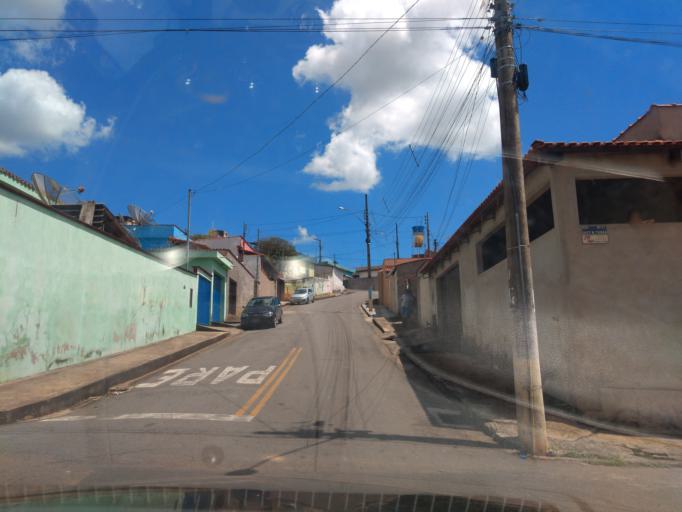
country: BR
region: Minas Gerais
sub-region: Tres Coracoes
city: Tres Coracoes
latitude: -21.6842
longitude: -45.2514
